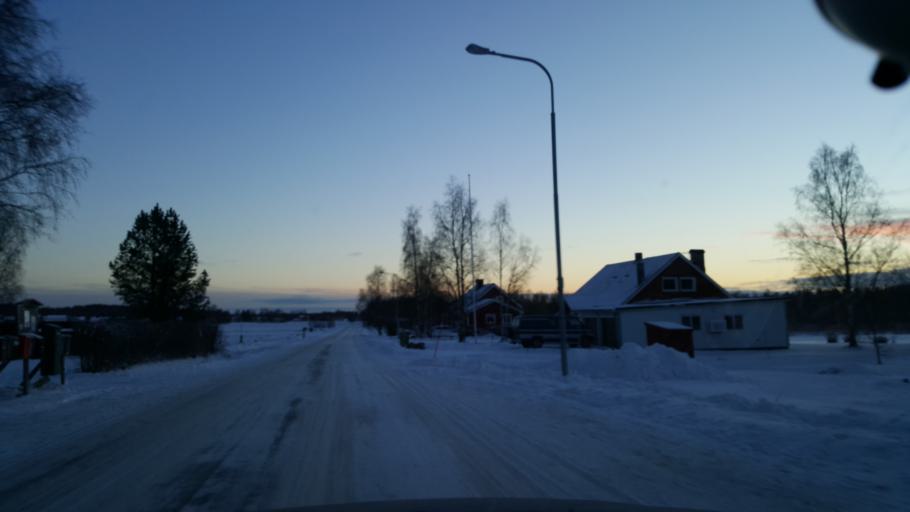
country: SE
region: Norrbotten
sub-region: Lulea Kommun
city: Sodra Sunderbyn
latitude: 65.5407
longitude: 21.9021
